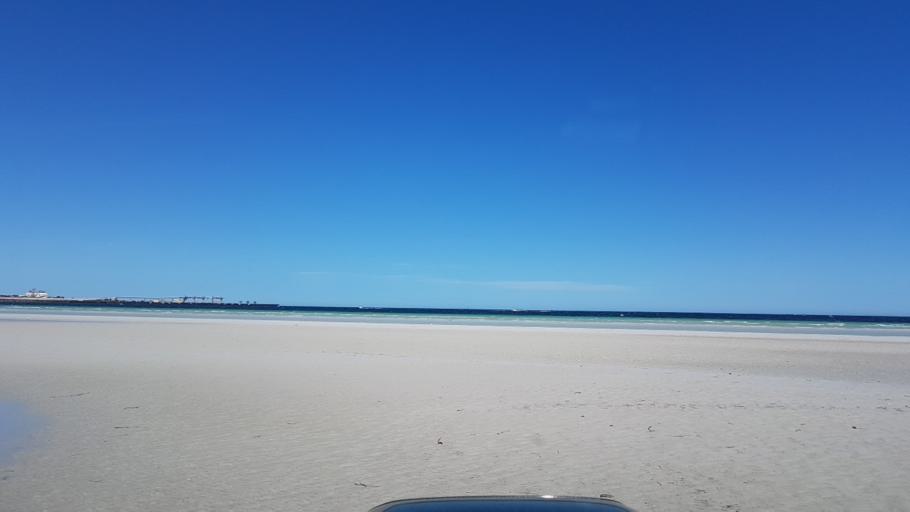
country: AU
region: South Australia
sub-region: Copper Coast
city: Wallaroo
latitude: -33.9120
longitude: 137.6297
